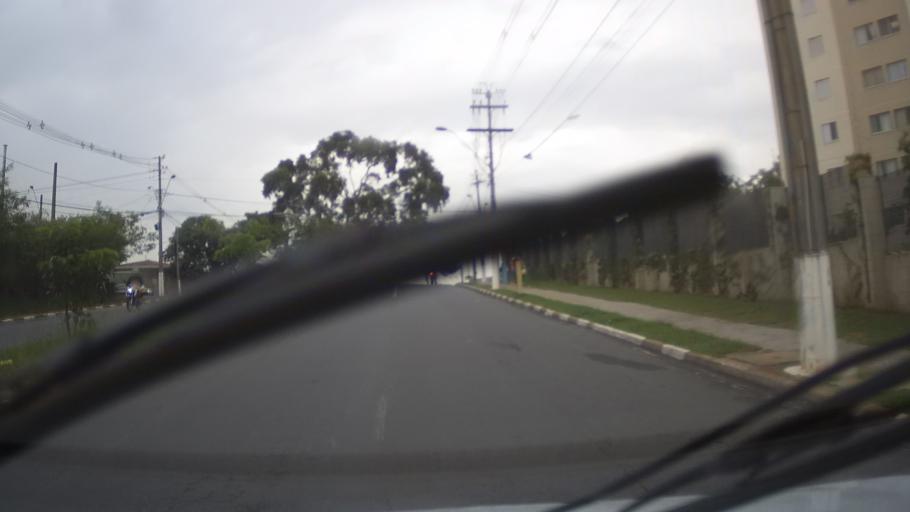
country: BR
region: Sao Paulo
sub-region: Campinas
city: Campinas
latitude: -22.9294
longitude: -47.0339
